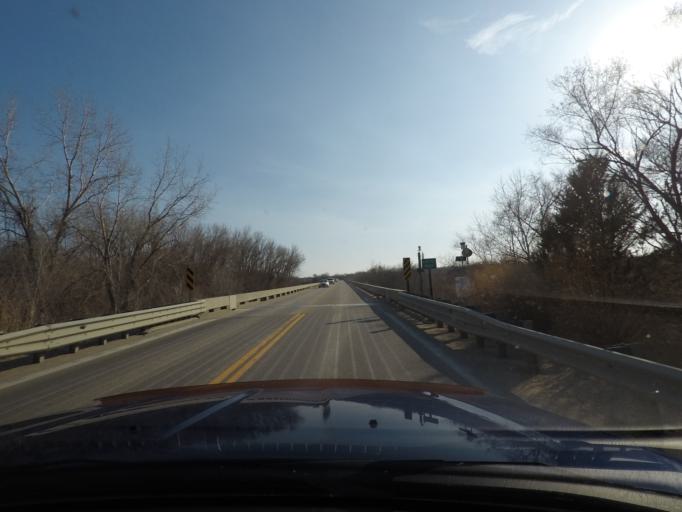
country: US
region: Kansas
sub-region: Douglas County
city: Lawrence
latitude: 39.0516
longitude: -95.3859
